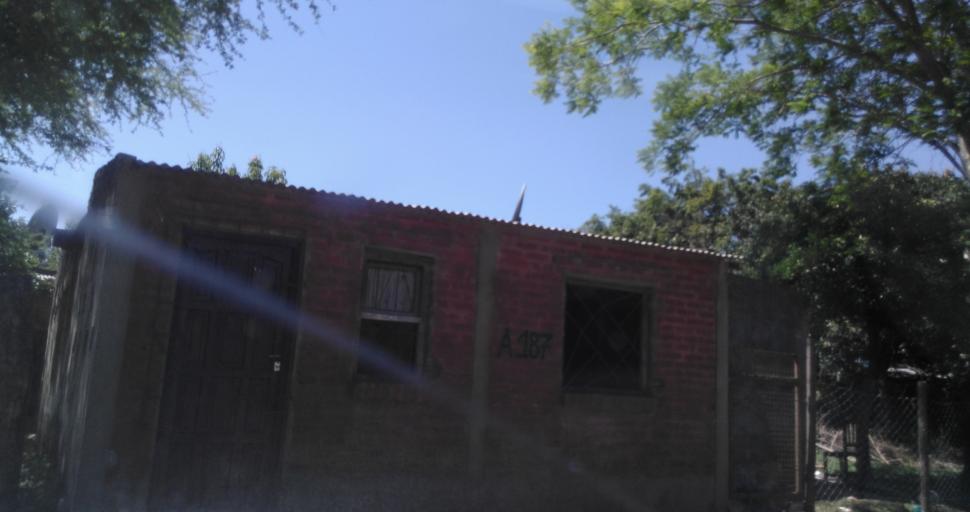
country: AR
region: Chaco
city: Resistencia
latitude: -27.4242
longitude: -58.9824
